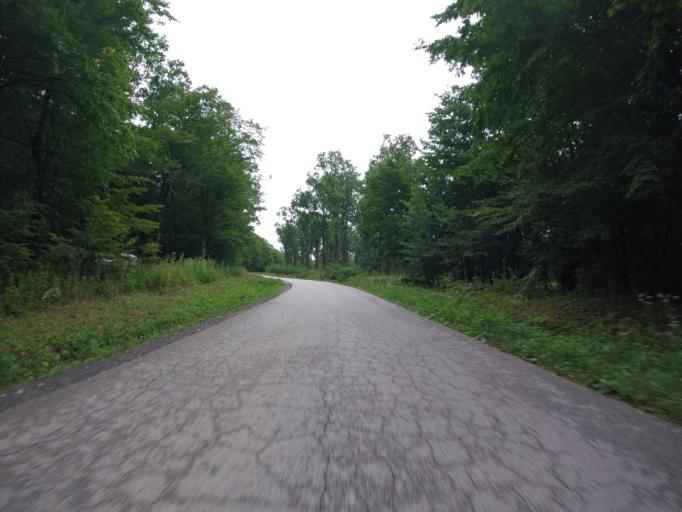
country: HR
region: Zagrebacka
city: Mraclin
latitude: 45.6154
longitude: 16.0941
